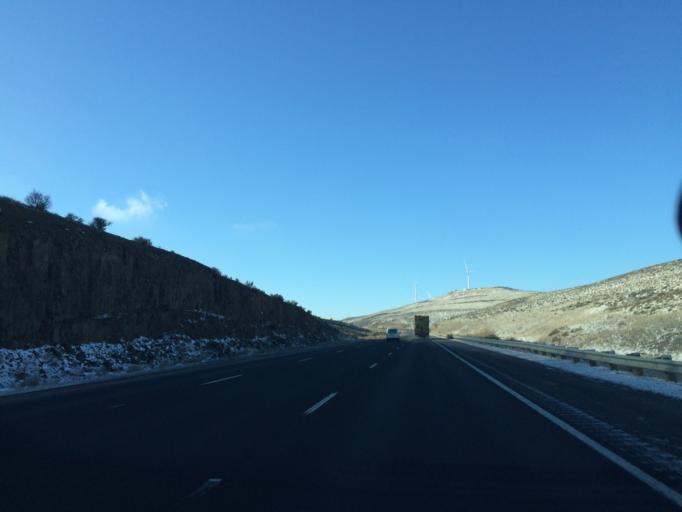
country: US
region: Washington
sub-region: Kittitas County
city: Kittitas
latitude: 46.9443
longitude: -120.1530
